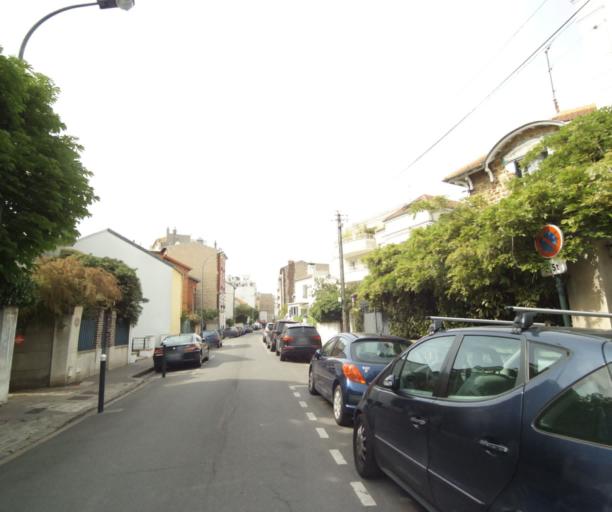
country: FR
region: Ile-de-France
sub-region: Departement des Hauts-de-Seine
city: Asnieres-sur-Seine
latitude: 48.9139
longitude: 2.2780
